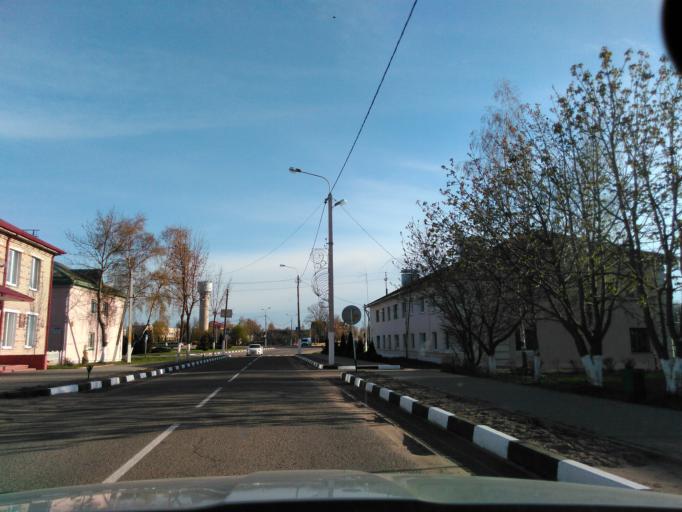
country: BY
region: Vitebsk
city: Chashniki
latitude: 54.8584
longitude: 29.1603
